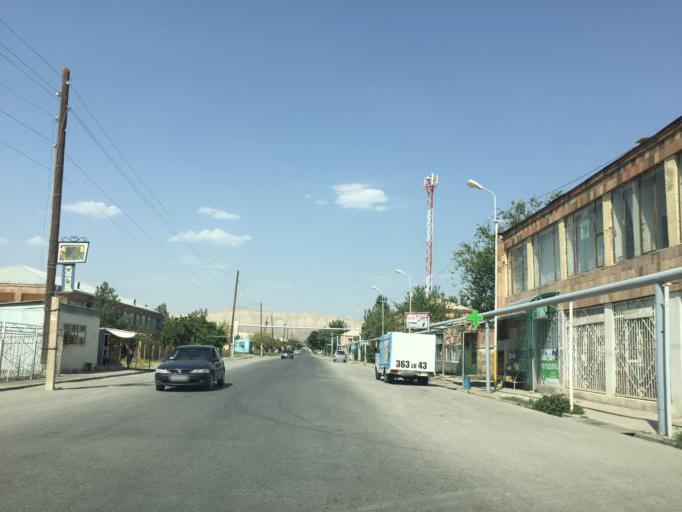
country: AM
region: Ararat
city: Shahumyan
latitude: 39.9024
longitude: 44.6020
